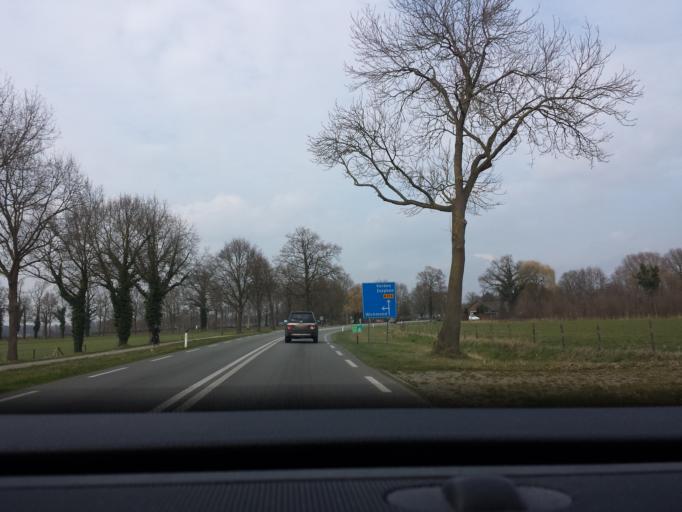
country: NL
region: Gelderland
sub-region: Gemeente Bronckhorst
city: Hengelo
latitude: 52.0667
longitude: 6.3086
